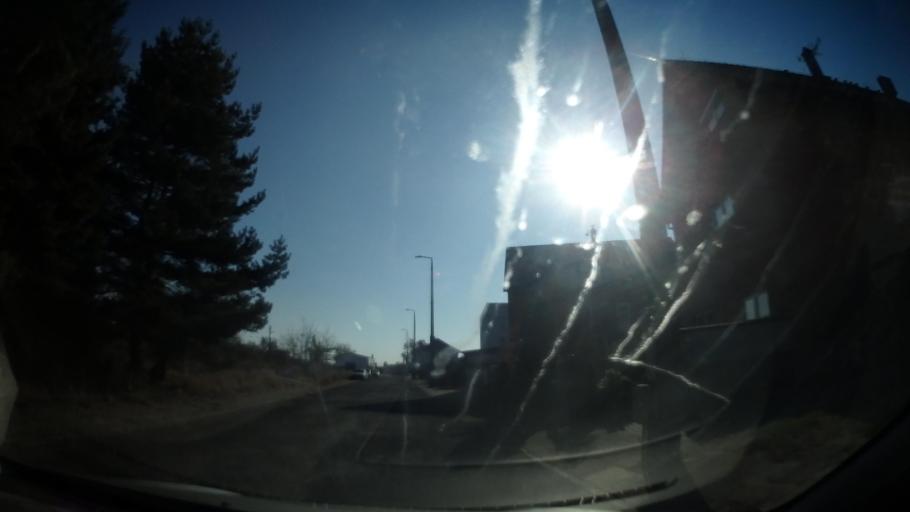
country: CZ
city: Tyniste nad Orlici
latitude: 50.1596
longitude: 16.0669
